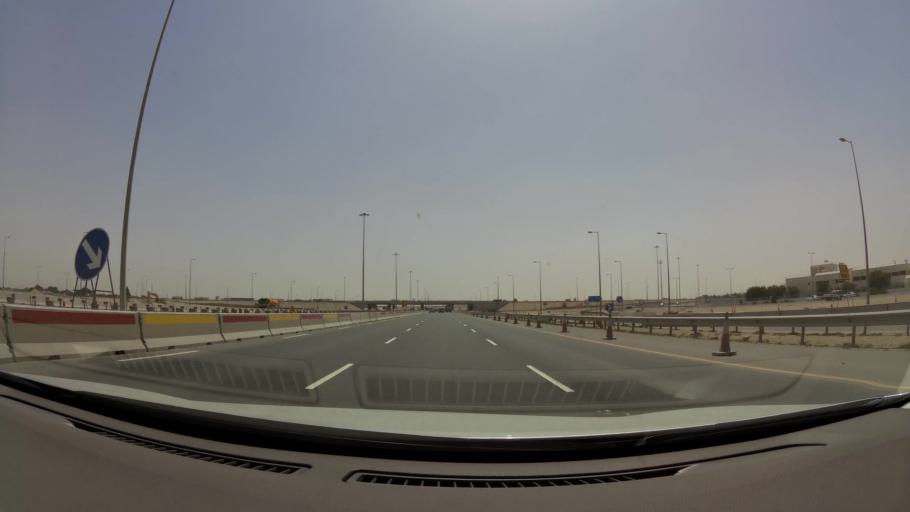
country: QA
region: Baladiyat Umm Salal
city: Umm Salal `Ali
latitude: 25.4519
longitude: 51.4094
